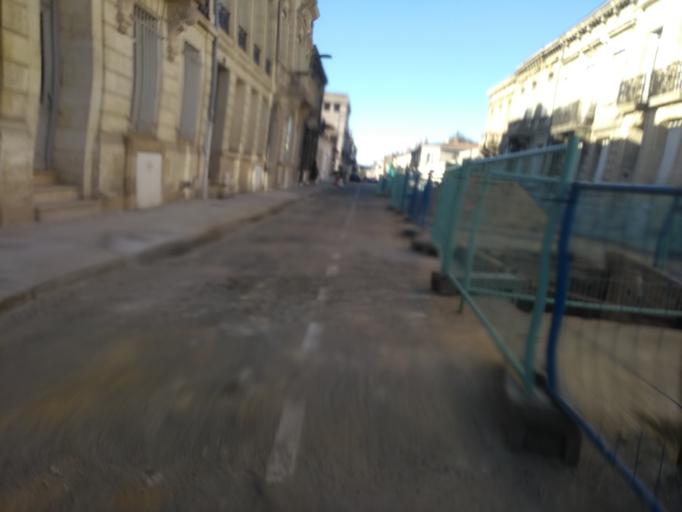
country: FR
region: Aquitaine
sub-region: Departement de la Gironde
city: Bordeaux
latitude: 44.8287
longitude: -0.5864
